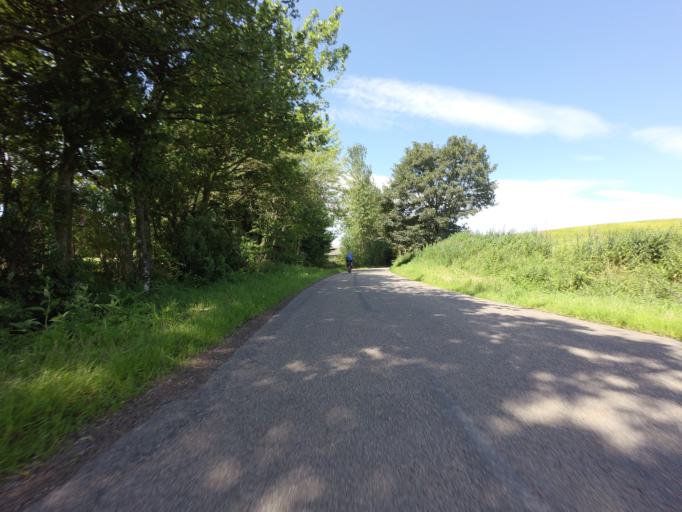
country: GB
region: Scotland
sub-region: Highland
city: Conon Bridge
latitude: 57.5541
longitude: -4.4073
